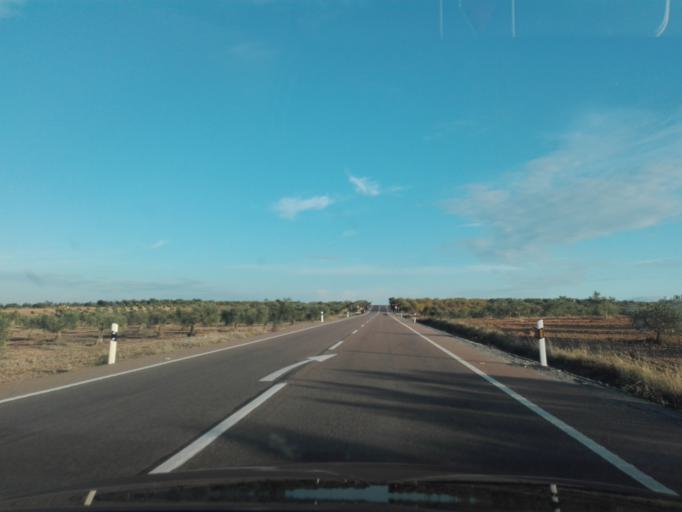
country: ES
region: Extremadura
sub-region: Provincia de Badajoz
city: Usagre
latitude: 38.3477
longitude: -6.1875
